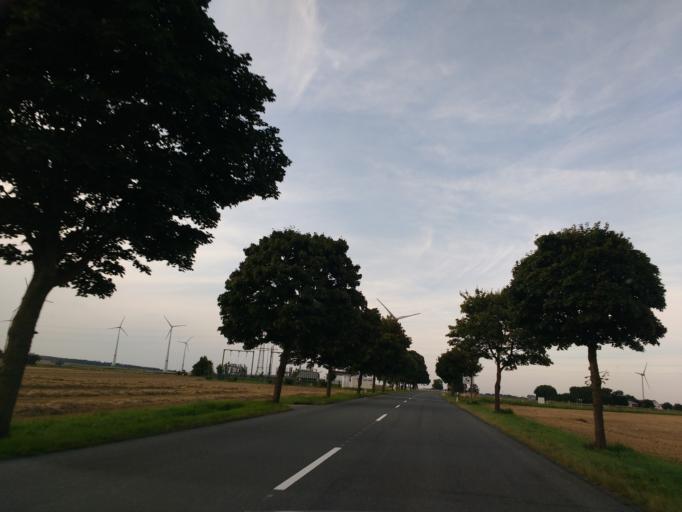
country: DE
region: North Rhine-Westphalia
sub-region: Regierungsbezirk Detmold
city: Wunnenberg
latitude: 51.5305
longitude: 8.7030
